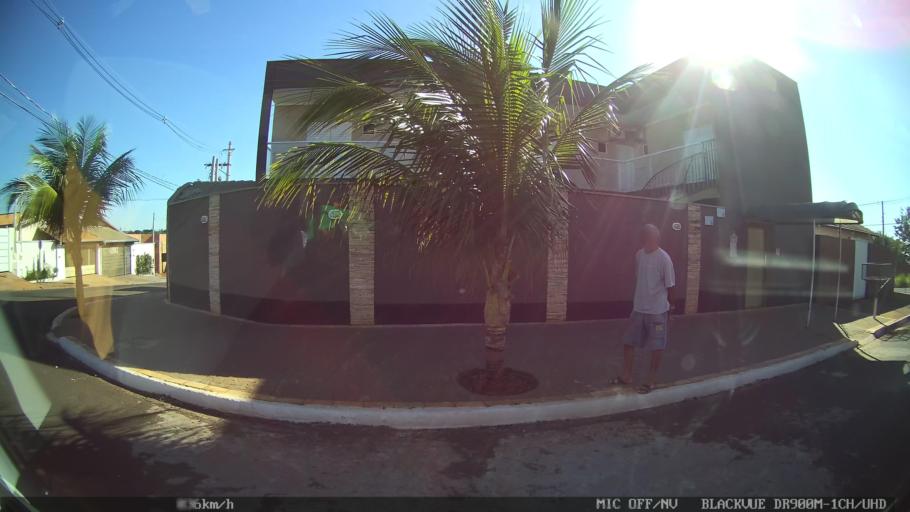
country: BR
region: Sao Paulo
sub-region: Olimpia
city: Olimpia
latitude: -20.7402
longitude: -48.8823
